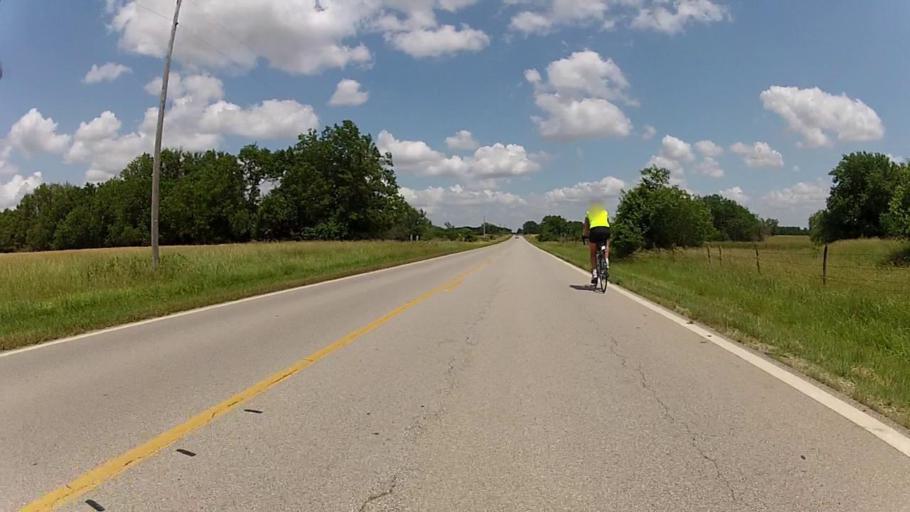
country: US
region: Kansas
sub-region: Labette County
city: Altamont
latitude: 37.1927
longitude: -95.3362
